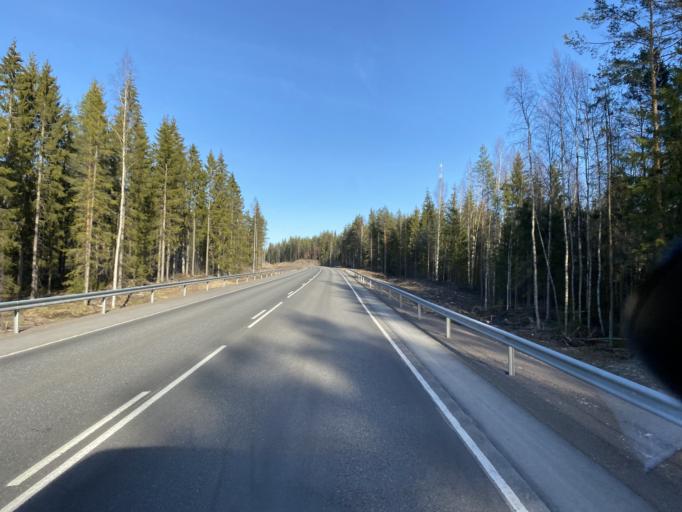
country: FI
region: Satakunta
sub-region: Pori
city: Huittinen
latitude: 61.1745
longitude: 22.5607
